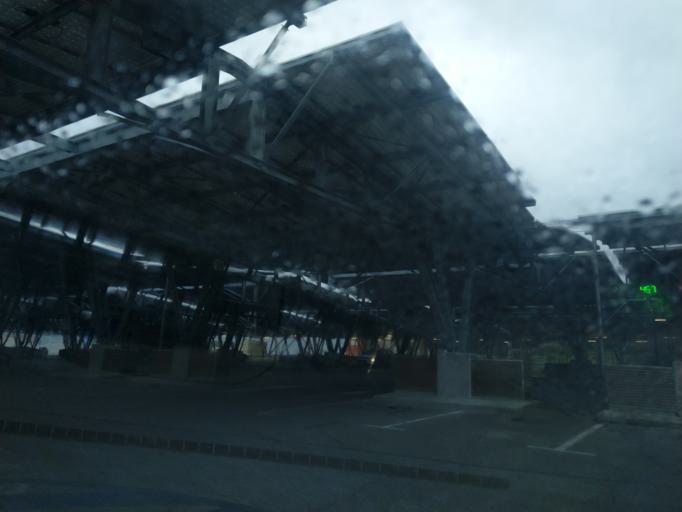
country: FR
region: Provence-Alpes-Cote d'Azur
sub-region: Departement des Bouches-du-Rhone
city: Septemes-les-Vallons
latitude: 43.4123
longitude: 5.3613
